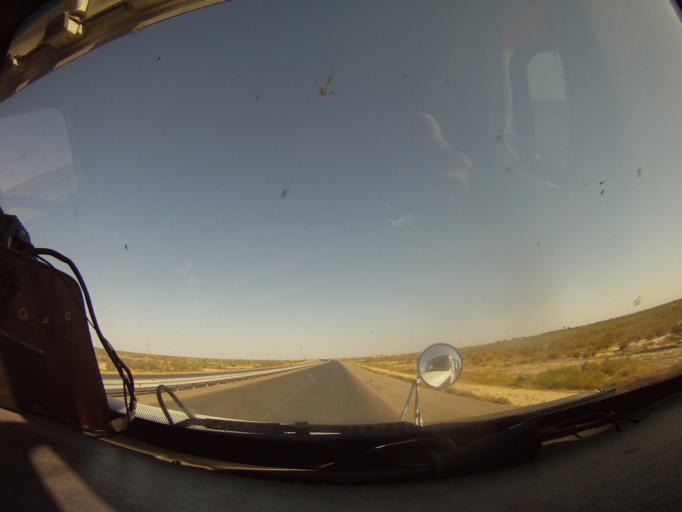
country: KZ
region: Qyzylorda
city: Belkol
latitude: 44.7841
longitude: 65.7436
